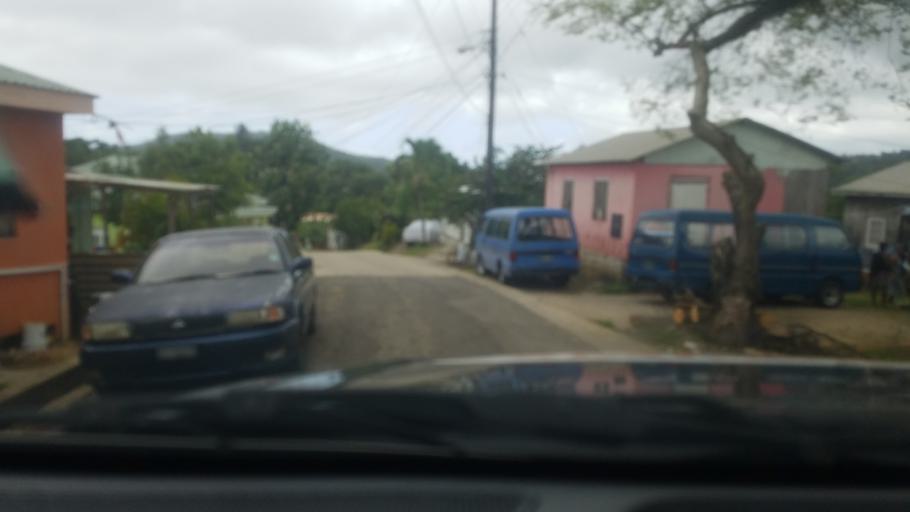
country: LC
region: Micoud Quarter
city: Micoud
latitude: 13.8059
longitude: -60.9471
